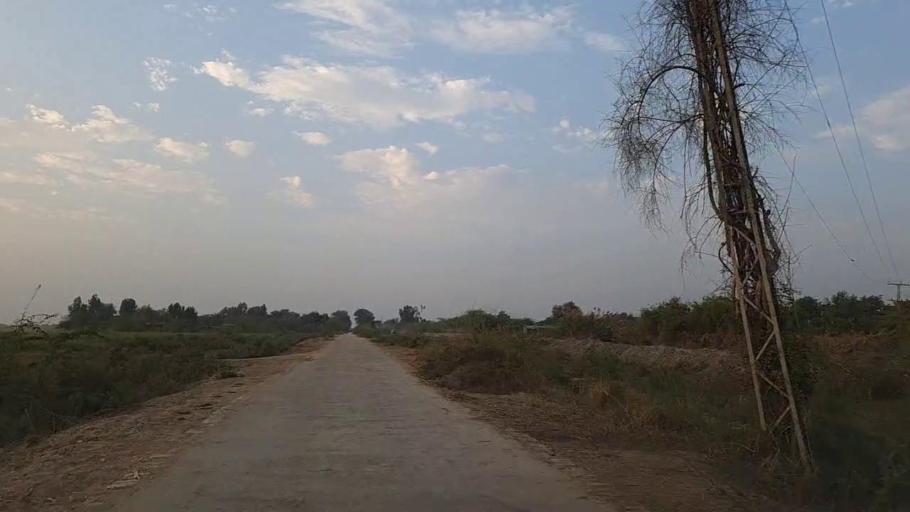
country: PK
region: Sindh
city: Mirwah Gorchani
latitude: 25.3394
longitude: 69.2080
